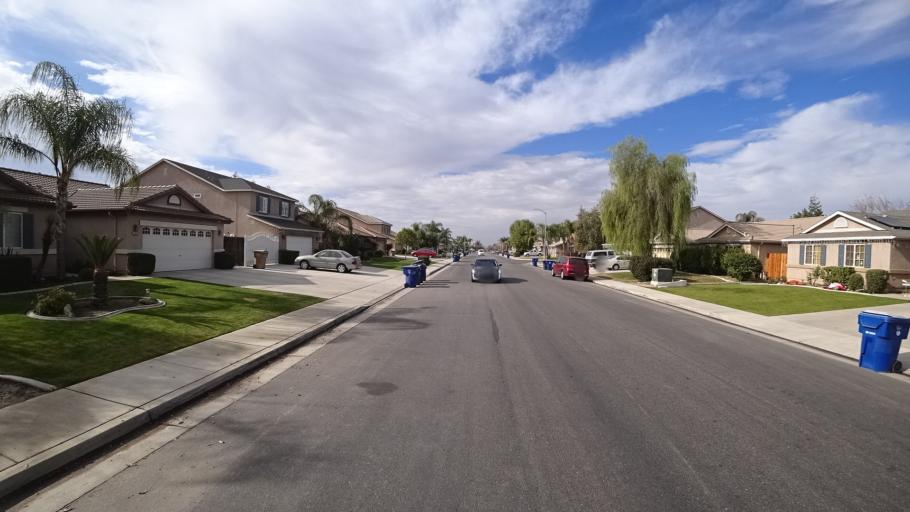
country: US
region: California
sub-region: Kern County
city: Rosedale
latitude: 35.4235
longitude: -119.1378
